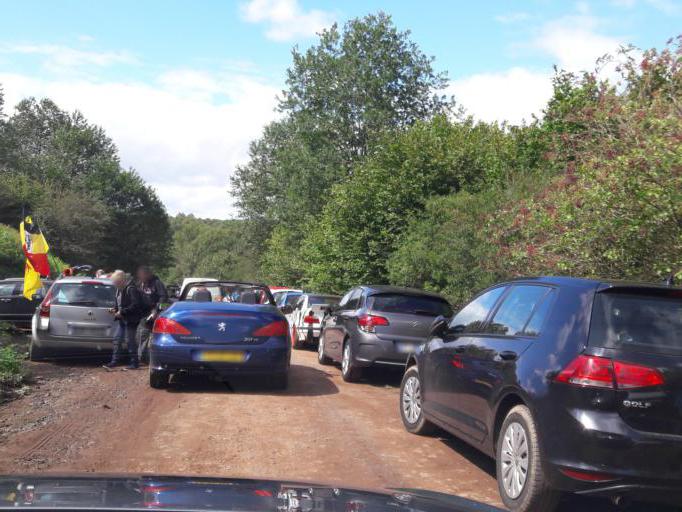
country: DE
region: Rheinland-Pfalz
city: Reichenbach
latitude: 49.6459
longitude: 7.3052
